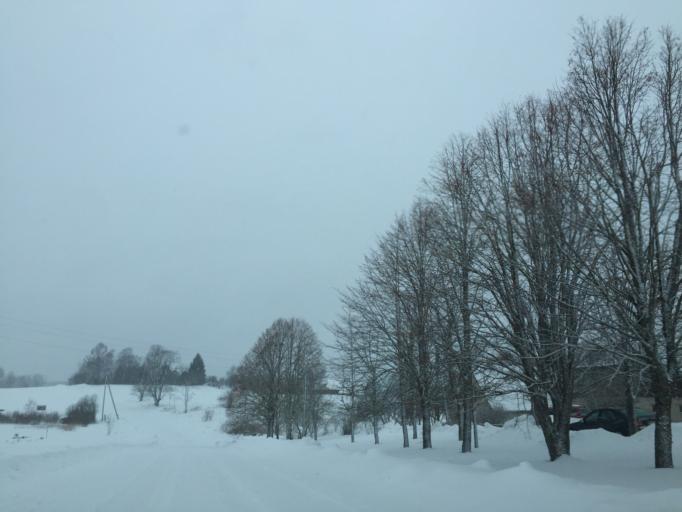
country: LV
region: Amatas Novads
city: Drabesi
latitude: 57.1688
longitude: 25.3193
